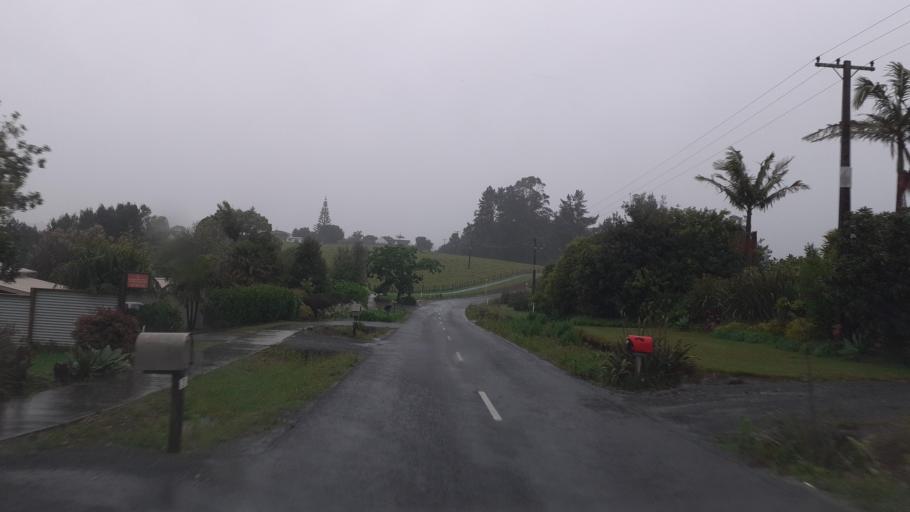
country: NZ
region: Northland
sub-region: Far North District
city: Kerikeri
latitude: -35.2008
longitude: 173.9756
